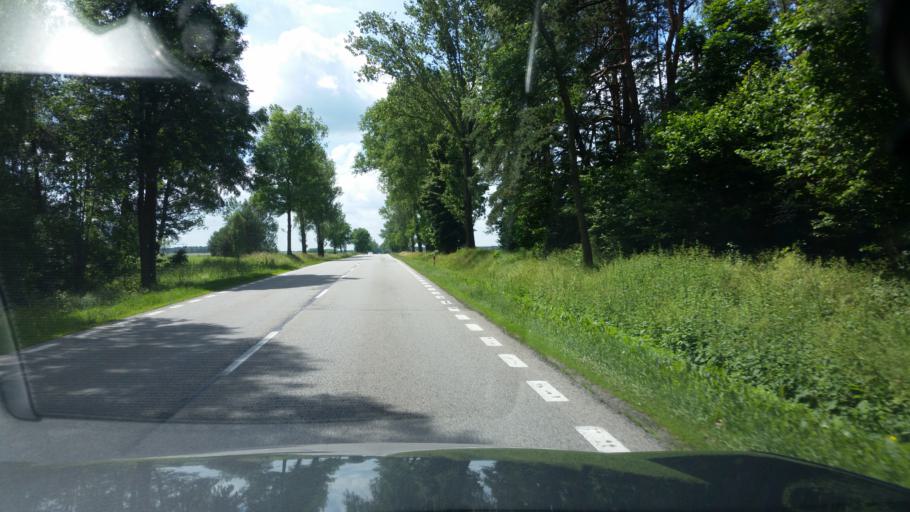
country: PL
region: Podlasie
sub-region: Powiat kolnenski
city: Stawiski
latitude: 53.3088
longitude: 22.1495
